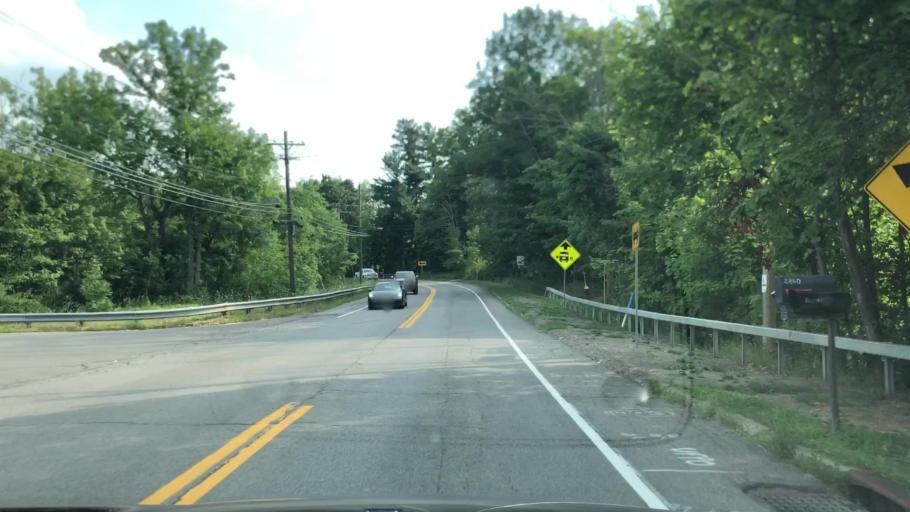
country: US
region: New York
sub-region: Erie County
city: Elma Center
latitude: 42.8483
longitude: -78.6410
